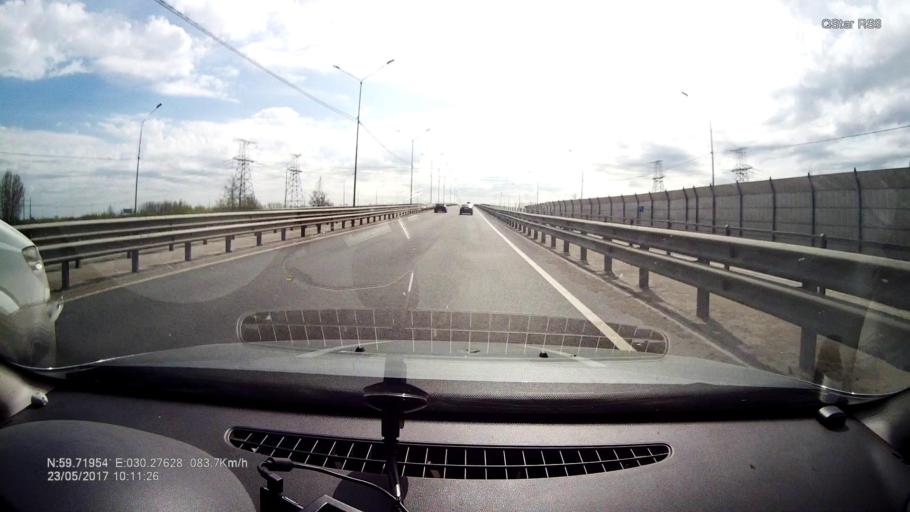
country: RU
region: St.-Petersburg
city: Aleksandrovskaya
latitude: 59.7195
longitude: 30.2765
